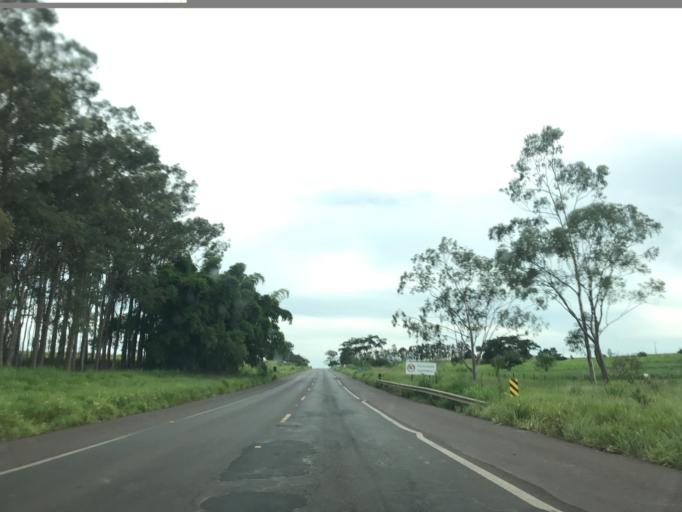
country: BR
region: Sao Paulo
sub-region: Tupa
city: Tupa
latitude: -21.6490
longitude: -50.5175
